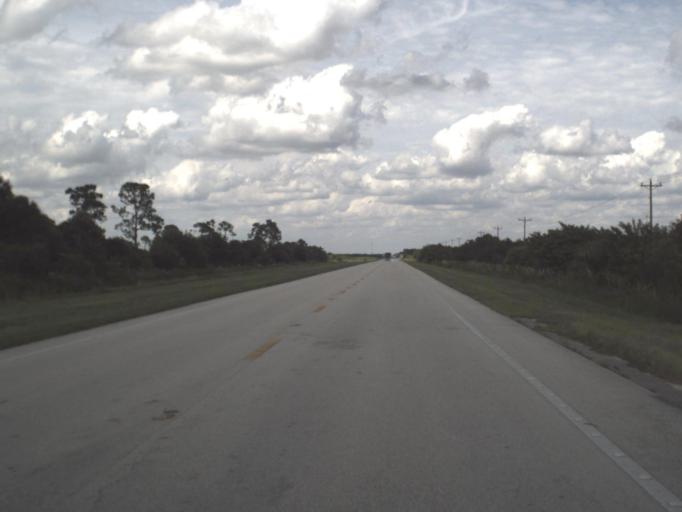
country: US
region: Florida
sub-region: Collier County
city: Immokalee
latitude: 26.5059
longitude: -81.4350
